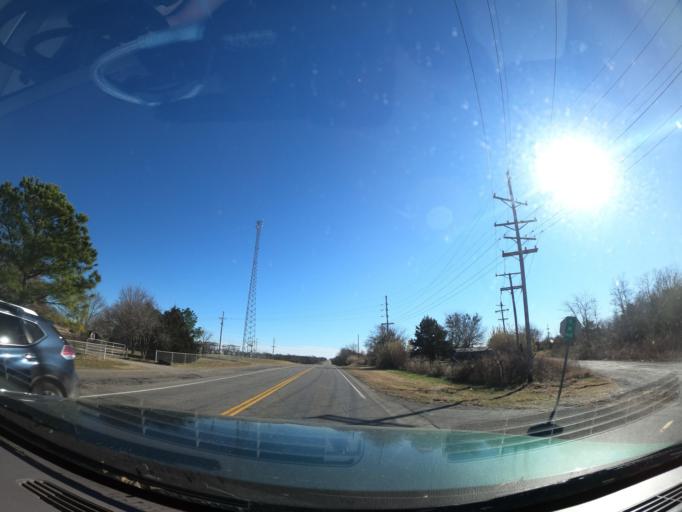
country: US
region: Oklahoma
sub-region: Muskogee County
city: Haskell
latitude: 35.7780
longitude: -95.6594
